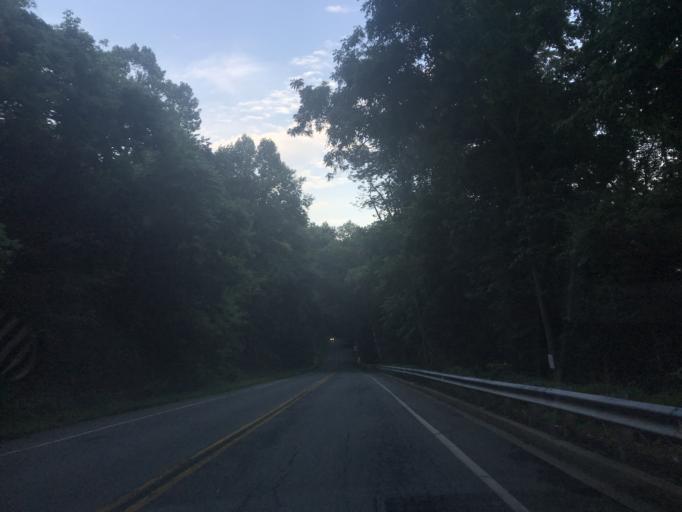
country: US
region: Maryland
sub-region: Cecil County
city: Rising Sun
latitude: 39.6670
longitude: -76.1685
